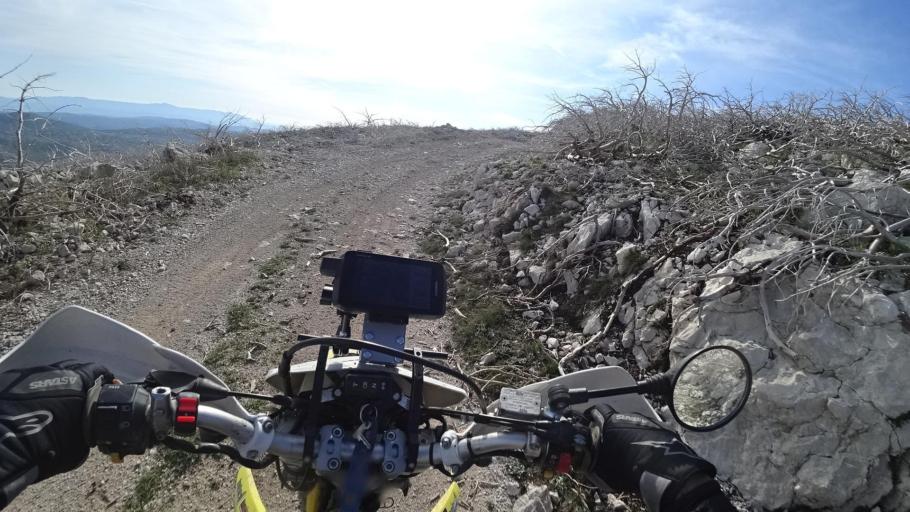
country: BA
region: Federation of Bosnia and Herzegovina
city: Kocerin
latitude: 43.5904
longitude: 17.5412
